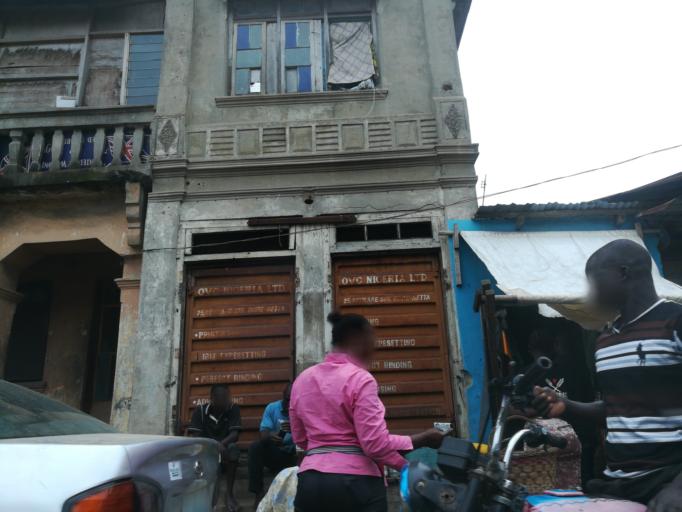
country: NG
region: Lagos
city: Ebute Metta
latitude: 6.4859
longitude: 3.3876
